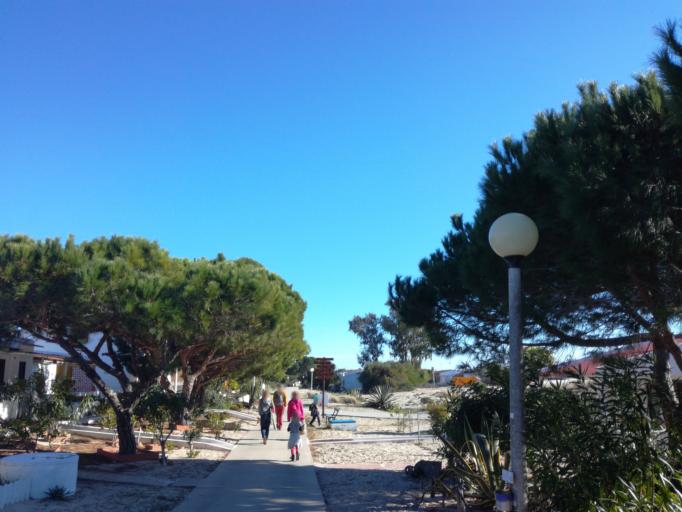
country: PT
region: Faro
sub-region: Olhao
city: Olhao
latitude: 37.0180
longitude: -7.8002
